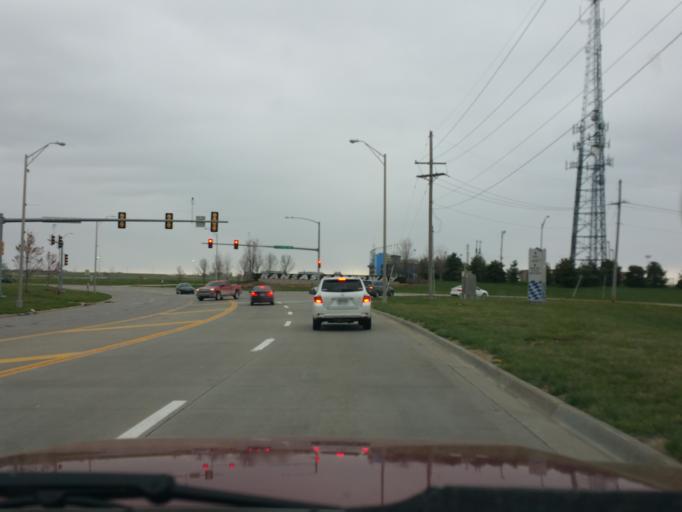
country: US
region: Kansas
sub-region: Wyandotte County
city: Edwardsville
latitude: 39.1076
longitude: -94.8350
